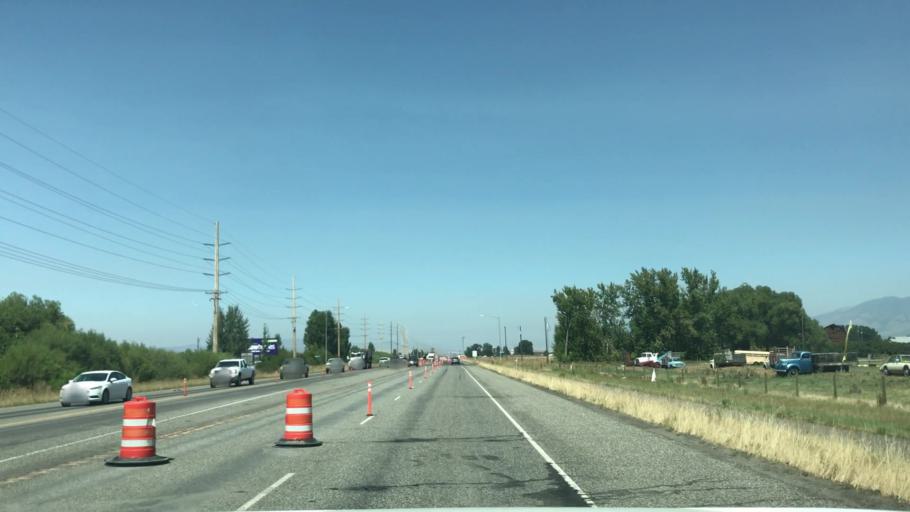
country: US
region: Montana
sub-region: Gallatin County
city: Belgrade
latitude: 45.7130
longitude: -111.1851
